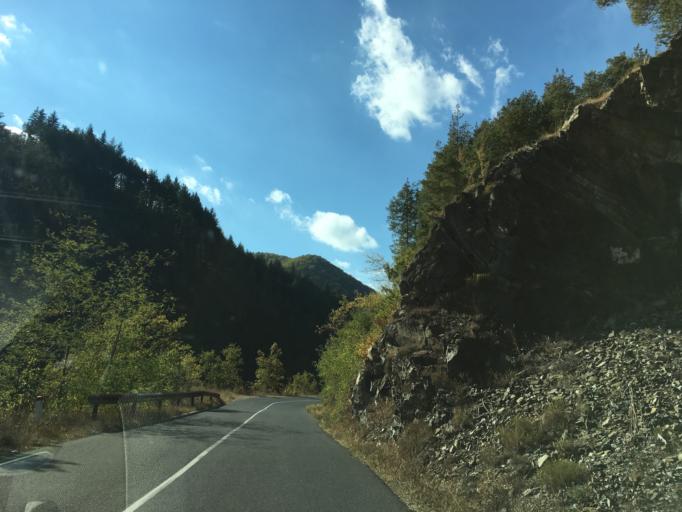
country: BG
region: Smolyan
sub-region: Obshtina Nedelino
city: Nedelino
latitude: 41.4350
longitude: 25.0302
